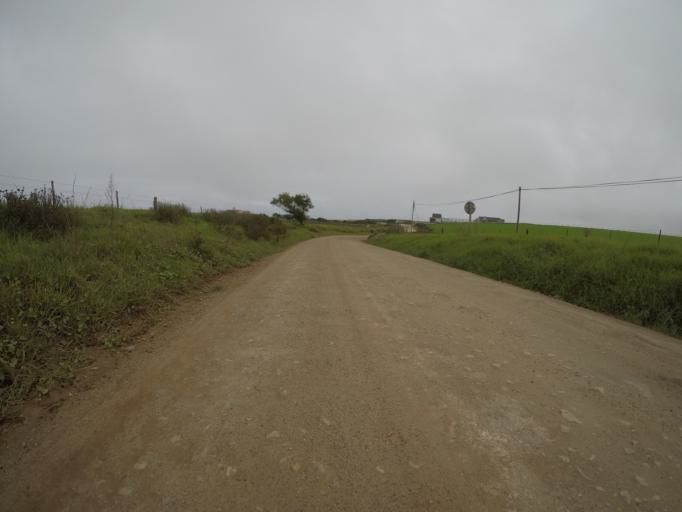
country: ZA
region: Eastern Cape
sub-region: Cacadu District Municipality
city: Kareedouw
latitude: -34.0699
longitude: 24.2368
